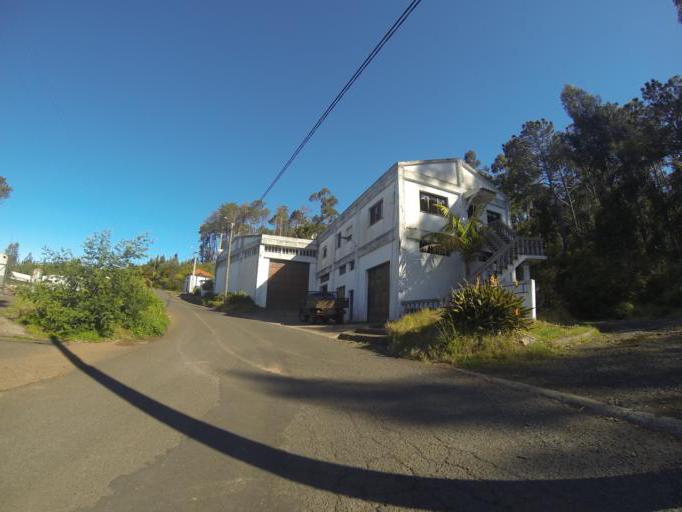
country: PT
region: Madeira
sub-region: Calheta
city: Estreito da Calheta
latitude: 32.7609
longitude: -17.1976
